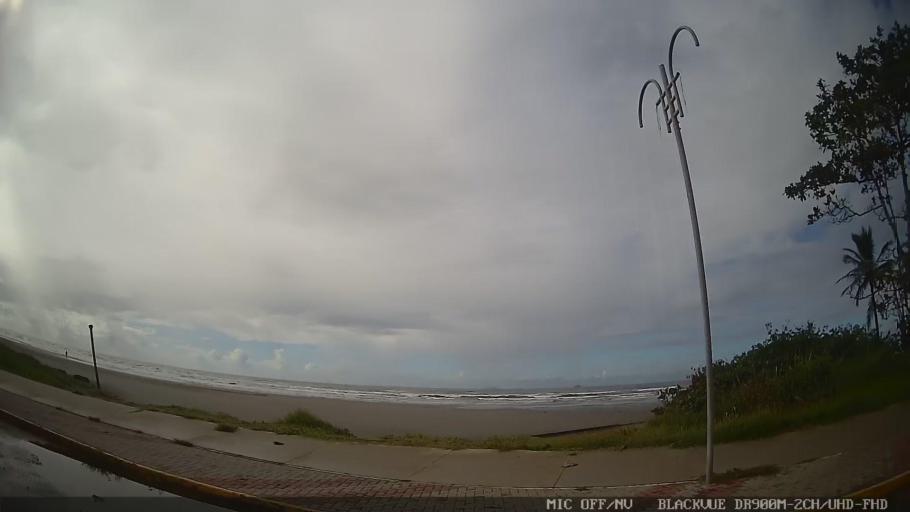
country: BR
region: Sao Paulo
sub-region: Itanhaem
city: Itanhaem
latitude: -24.2424
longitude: -46.8846
